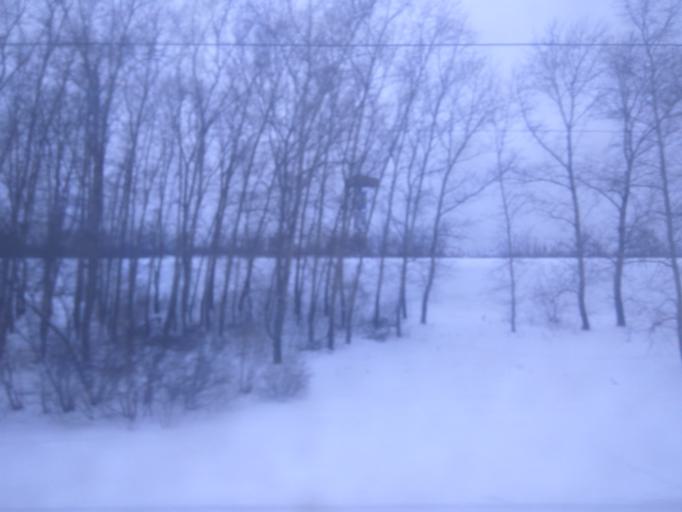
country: RU
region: Moscow
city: Tekstil'shchiki
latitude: 55.6988
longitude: 37.7303
